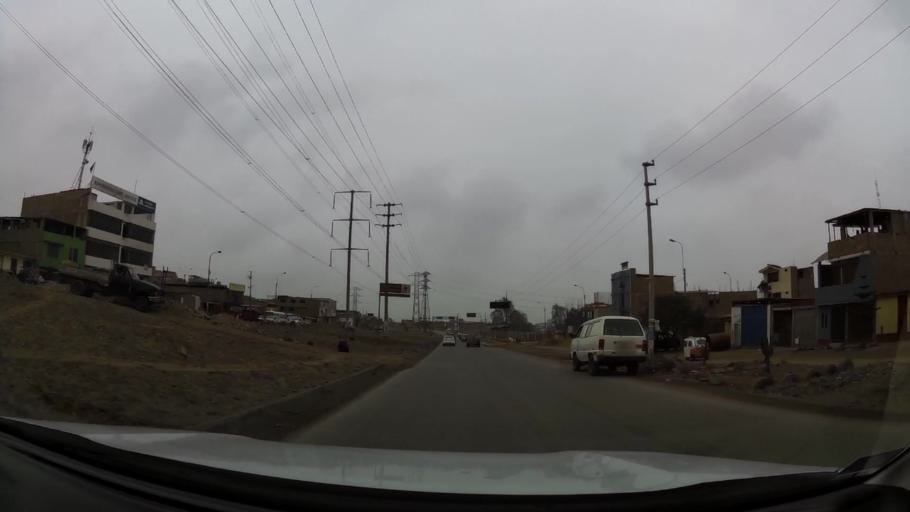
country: PE
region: Lima
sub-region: Lima
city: Surco
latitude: -12.2227
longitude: -76.9202
